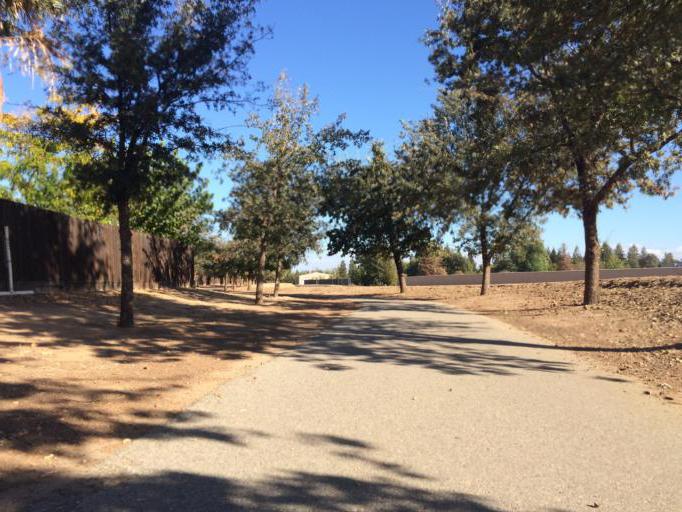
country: US
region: California
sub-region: Fresno County
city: Clovis
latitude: 36.8636
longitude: -119.6794
